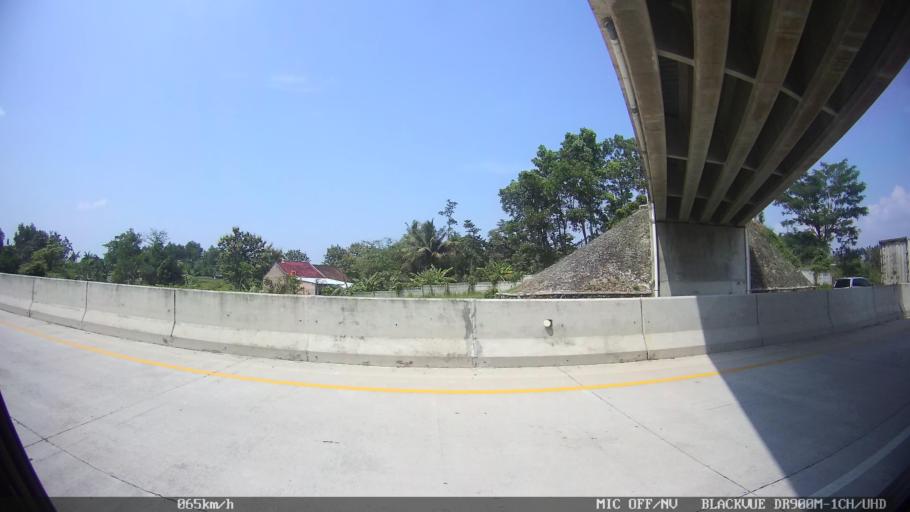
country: ID
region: Lampung
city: Kedaton
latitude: -5.3350
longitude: 105.2996
